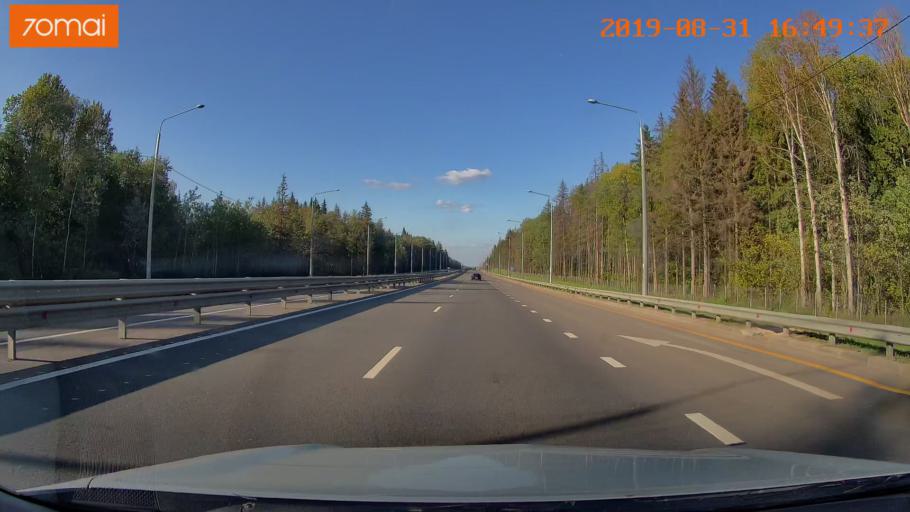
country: RU
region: Kaluga
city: Pyatovskiy
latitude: 54.6936
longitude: 36.1561
